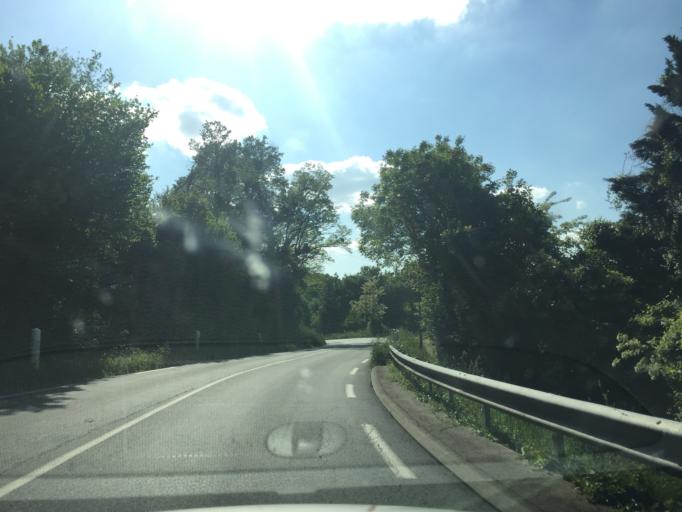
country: FR
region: Aquitaine
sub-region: Departement de la Gironde
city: Rauzan
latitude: 44.8072
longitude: -0.1409
